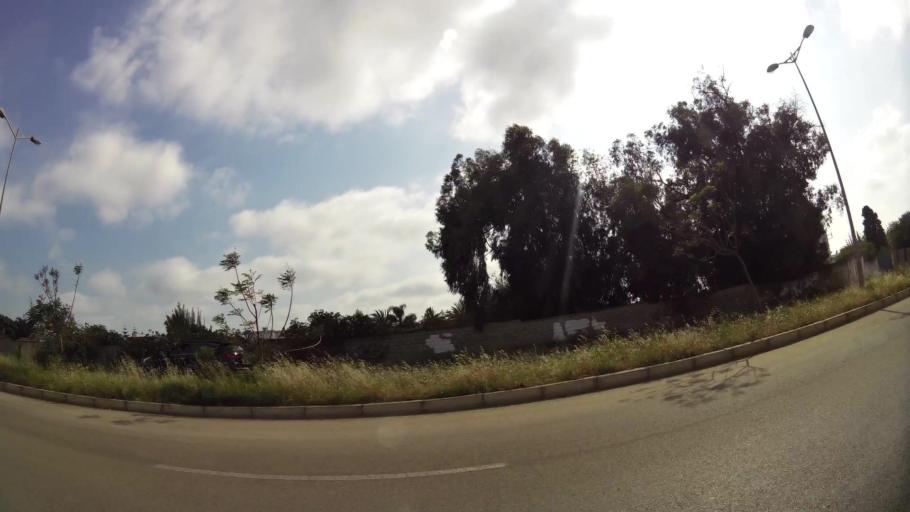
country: MA
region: Rabat-Sale-Zemmour-Zaer
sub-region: Rabat
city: Rabat
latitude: 33.9712
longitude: -6.8517
